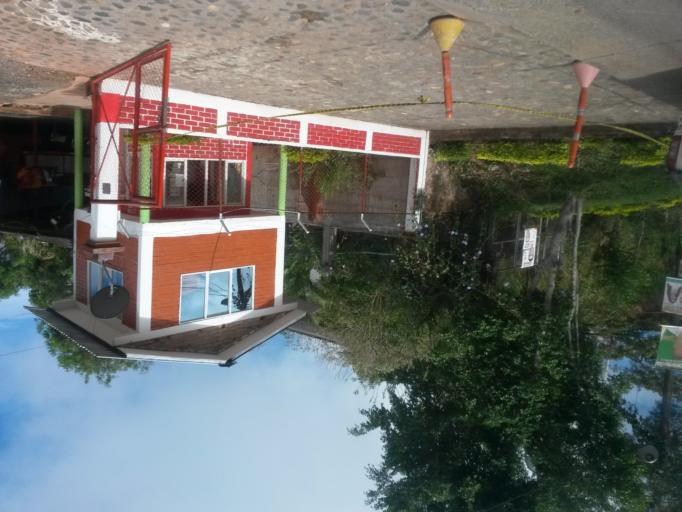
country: CO
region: Cauca
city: El Bordo
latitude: 2.1186
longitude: -76.9830
